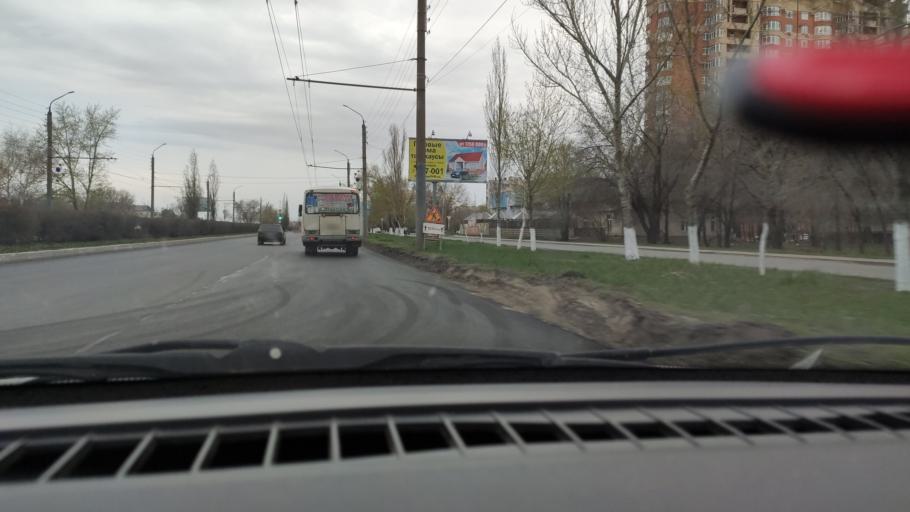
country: RU
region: Orenburg
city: Orenburg
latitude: 51.8140
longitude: 55.1073
